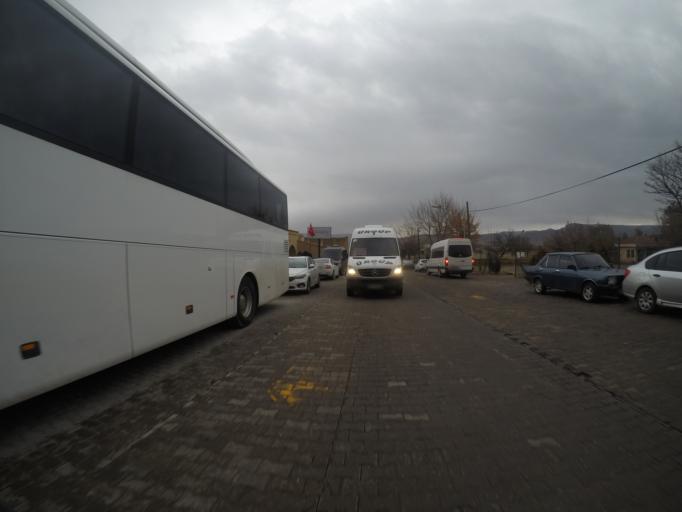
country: TR
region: Nevsehir
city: Urgub
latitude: 38.6331
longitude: 34.9036
